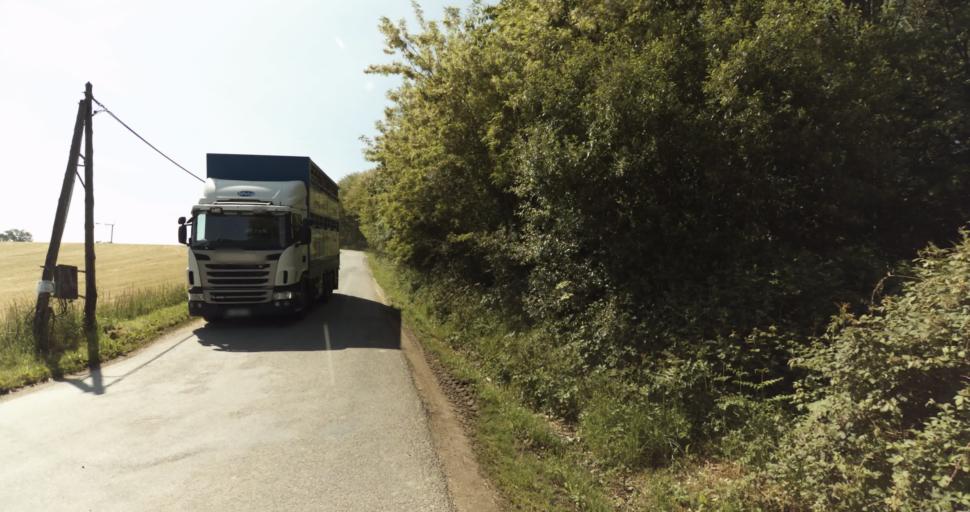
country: FR
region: Limousin
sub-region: Departement de la Haute-Vienne
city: Solignac
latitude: 45.7298
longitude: 1.2655
